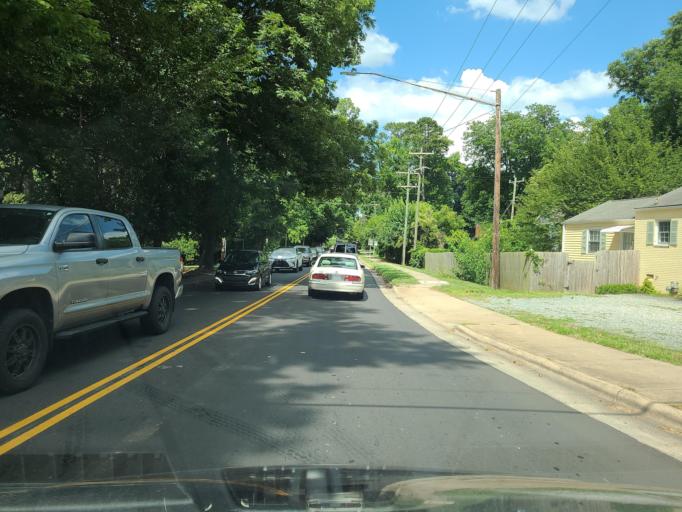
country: US
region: North Carolina
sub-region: Mecklenburg County
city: Charlotte
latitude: 35.2098
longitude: -80.7947
